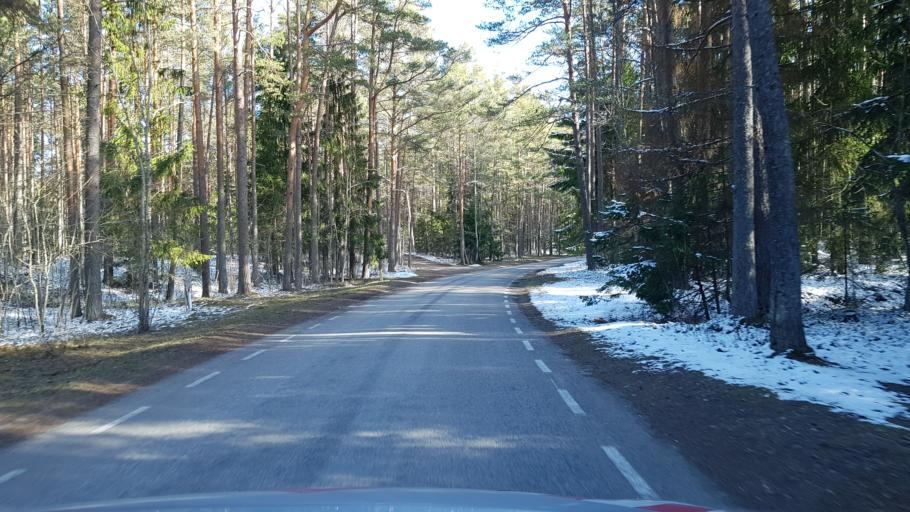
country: EE
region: Harju
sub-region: Loksa linn
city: Loksa
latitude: 59.5791
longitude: 25.9739
